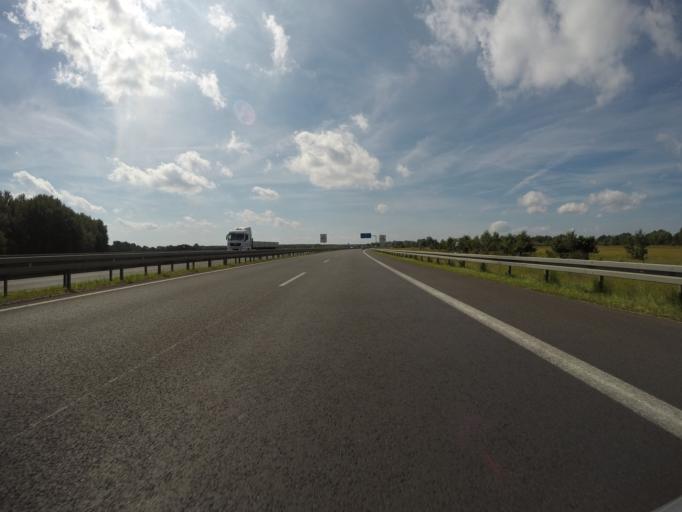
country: DE
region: Brandenburg
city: Leegebruch
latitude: 52.7164
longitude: 13.2170
